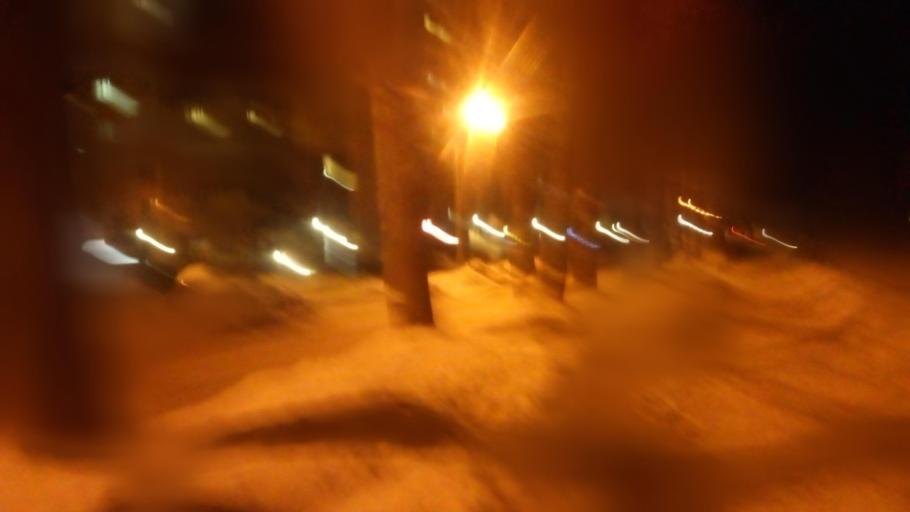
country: RU
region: Novosibirsk
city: Akademgorodok
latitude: 54.8699
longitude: 83.0864
